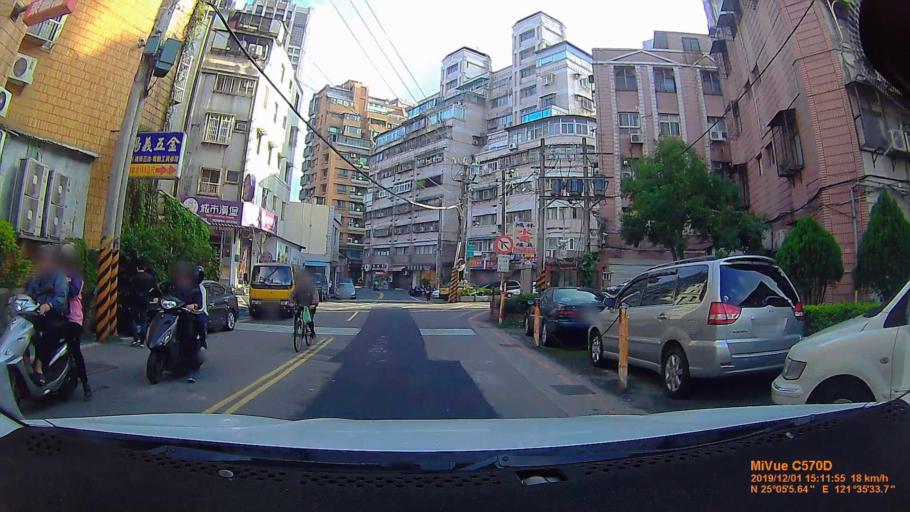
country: TW
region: Taipei
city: Taipei
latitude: 25.0848
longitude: 121.5927
